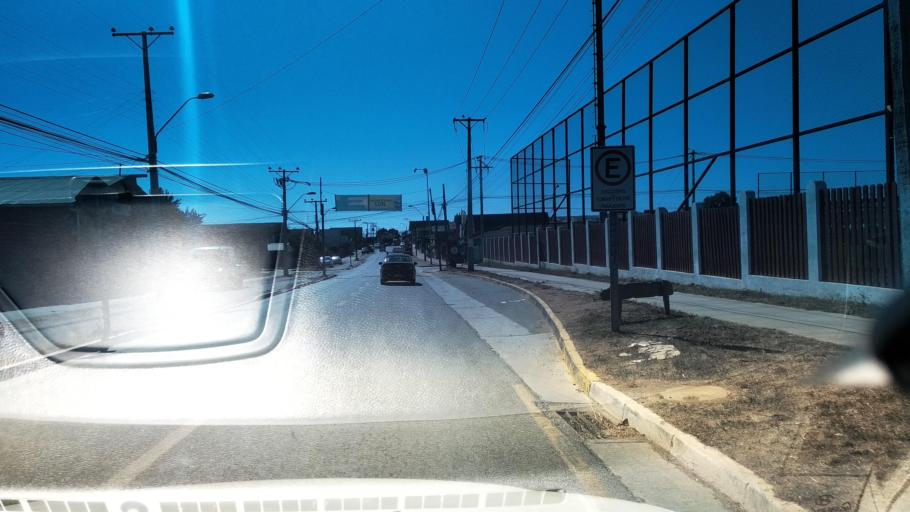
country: CL
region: O'Higgins
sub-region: Provincia de Colchagua
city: Santa Cruz
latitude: -34.3935
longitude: -71.9957
